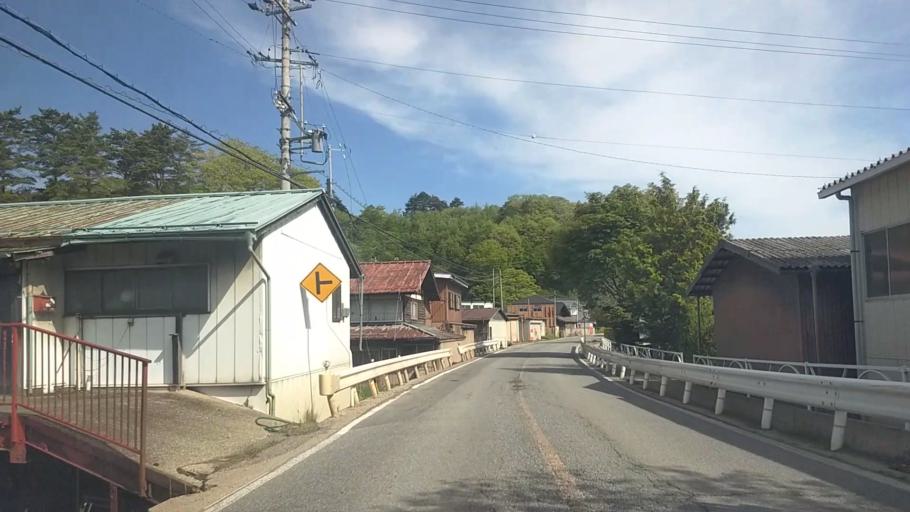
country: JP
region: Nagano
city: Saku
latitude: 36.0385
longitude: 138.4723
